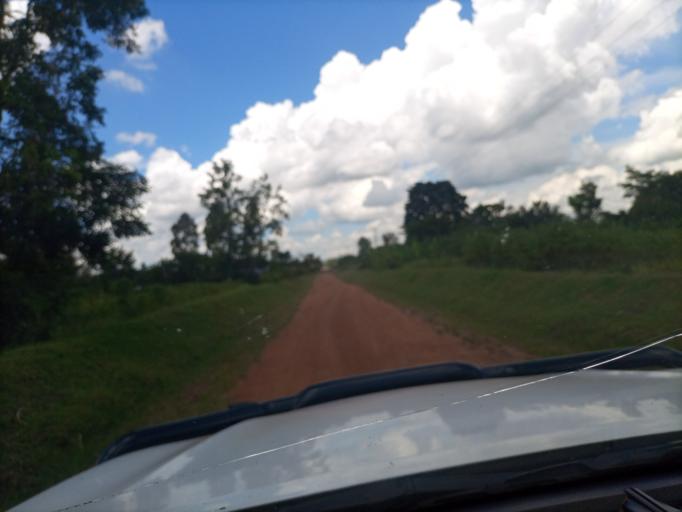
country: UG
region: Eastern Region
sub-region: Tororo District
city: Tororo
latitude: 0.6746
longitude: 34.0052
